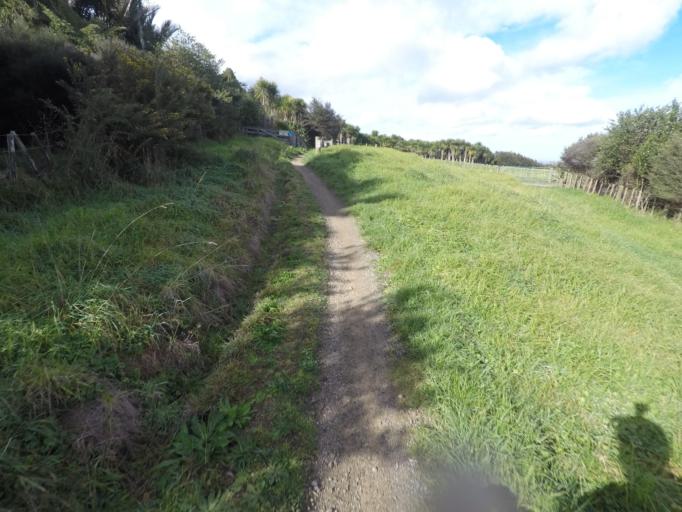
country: NZ
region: Auckland
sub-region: Auckland
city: Manukau City
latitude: -36.9980
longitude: 174.9143
